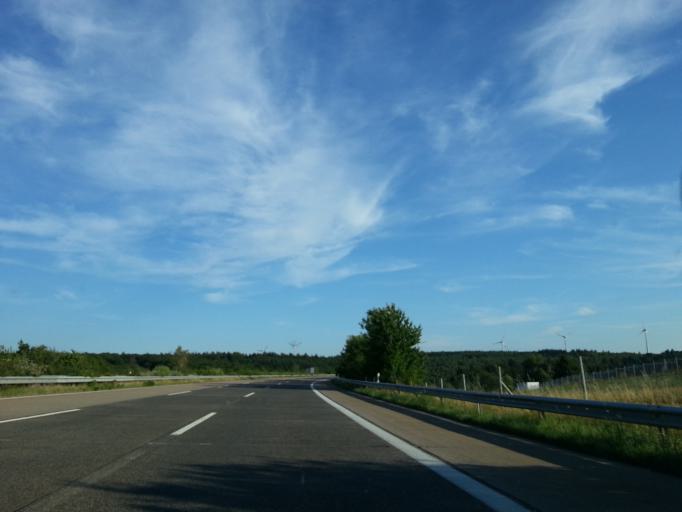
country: DE
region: Rheinland-Pfalz
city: Polich
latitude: 49.7737
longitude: 6.8535
